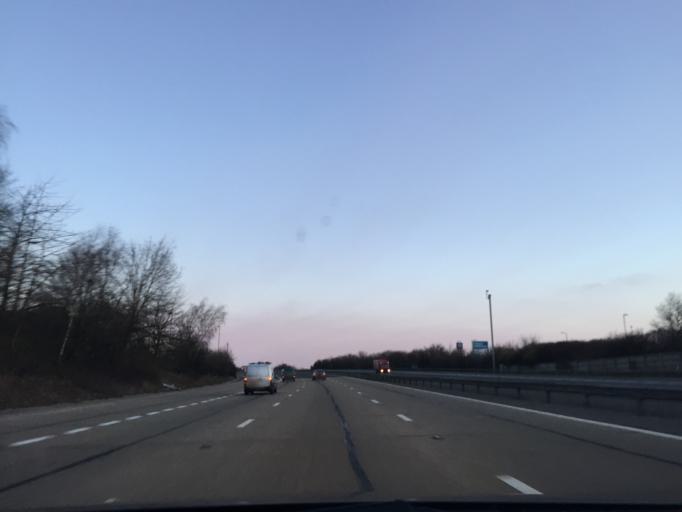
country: GB
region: England
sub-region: Hampshire
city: Eastleigh
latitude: 50.9446
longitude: -1.3639
